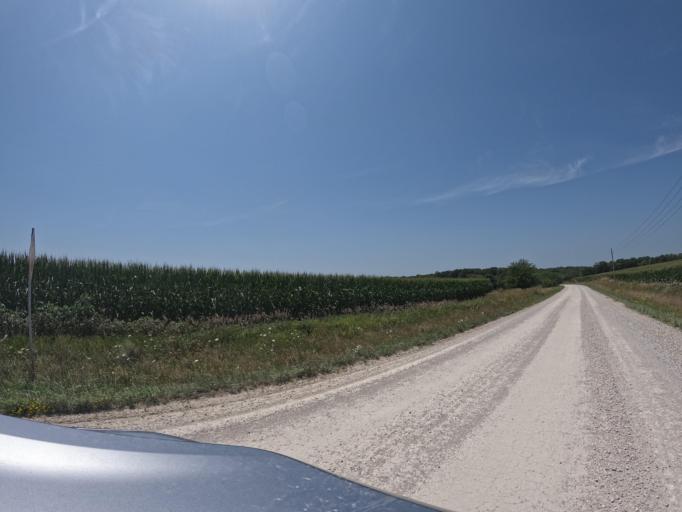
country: US
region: Iowa
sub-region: Henry County
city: Mount Pleasant
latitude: 40.9270
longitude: -91.6250
